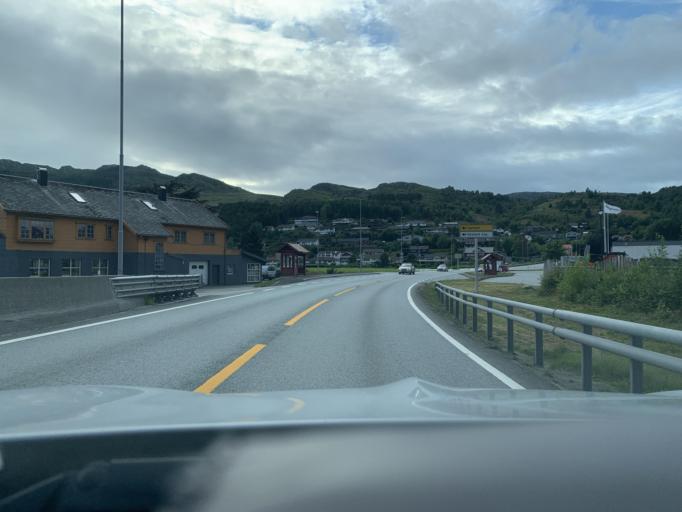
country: NO
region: Rogaland
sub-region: Bjerkreim
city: Vikesa
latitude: 58.6301
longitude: 6.0792
